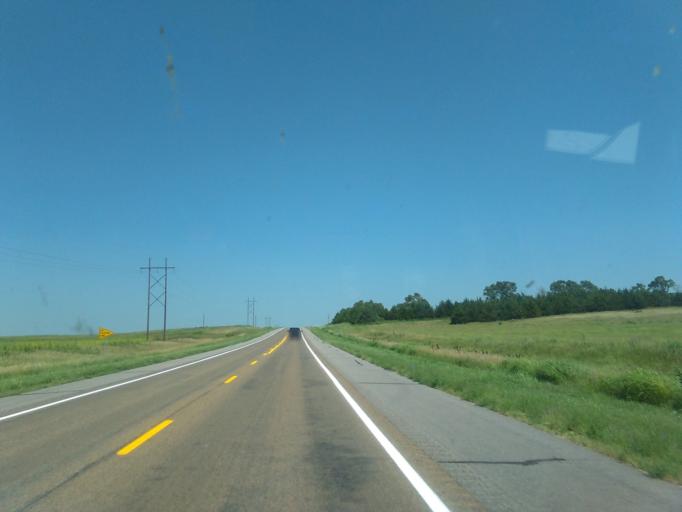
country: US
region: Nebraska
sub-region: Lincoln County
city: North Platte
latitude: 40.7913
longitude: -100.7537
